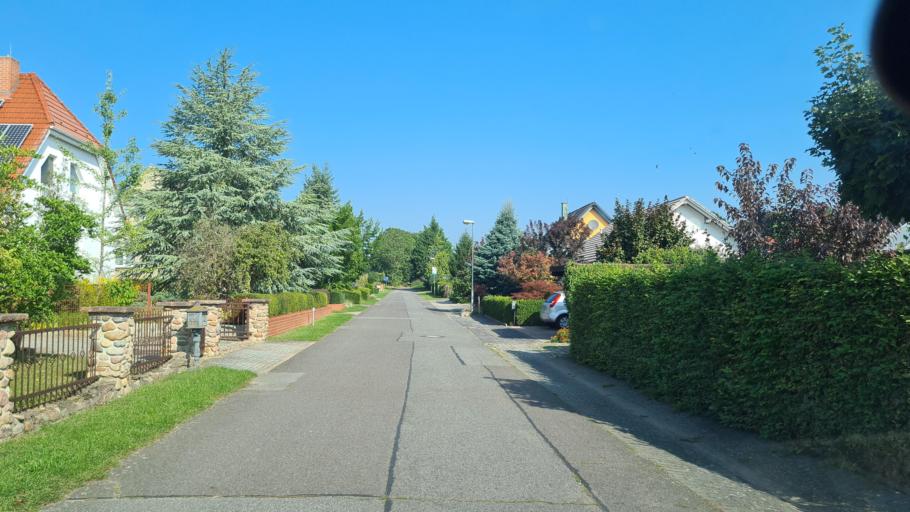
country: DE
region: Brandenburg
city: Luckau
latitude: 51.8400
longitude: 13.6890
